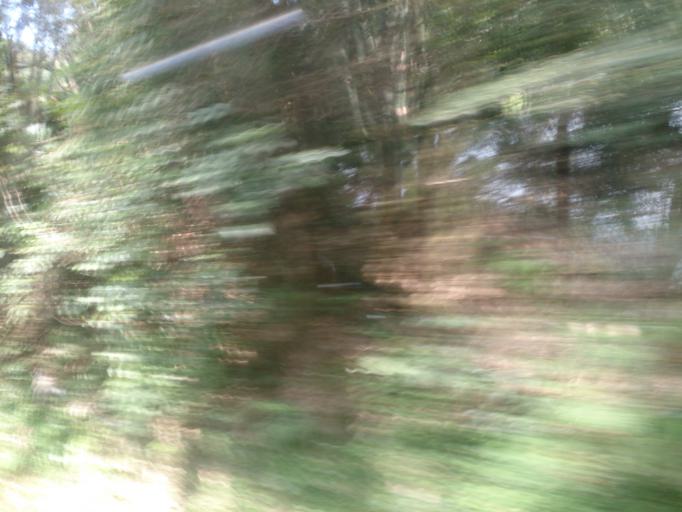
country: TW
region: Taipei
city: Taipei
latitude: 25.1647
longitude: 121.5439
